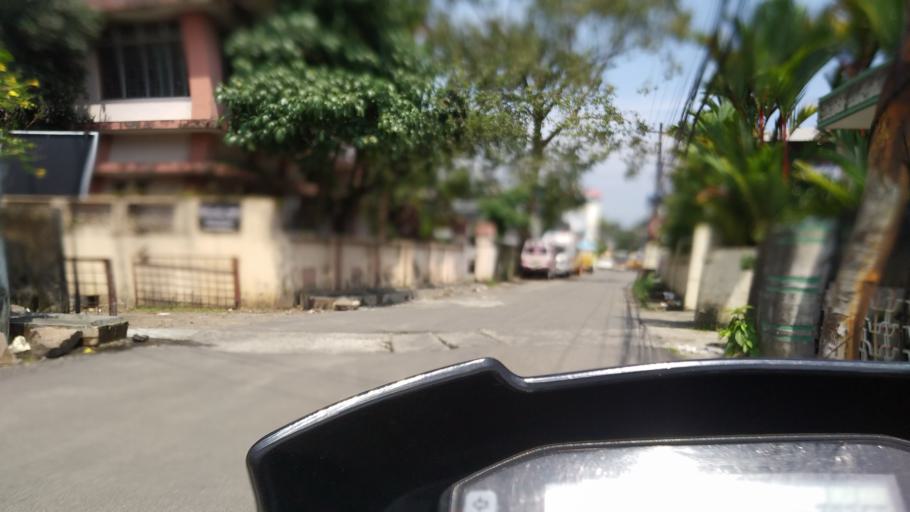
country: IN
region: Kerala
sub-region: Ernakulam
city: Cochin
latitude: 9.9706
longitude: 76.2878
